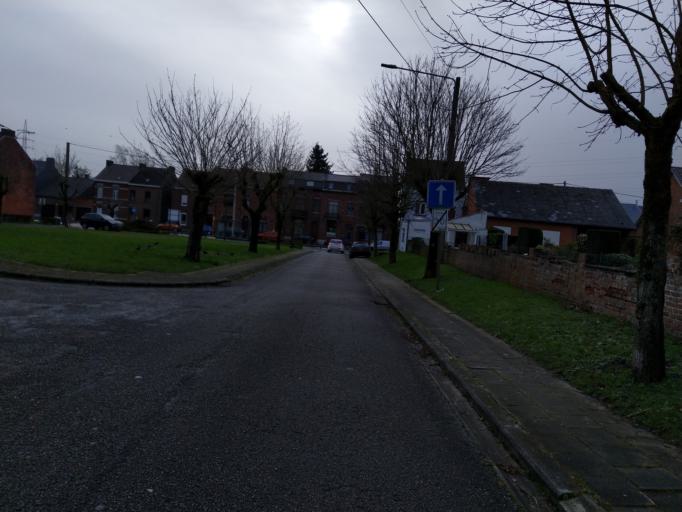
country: BE
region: Wallonia
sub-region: Province du Hainaut
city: Mons
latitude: 50.4862
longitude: 3.9586
